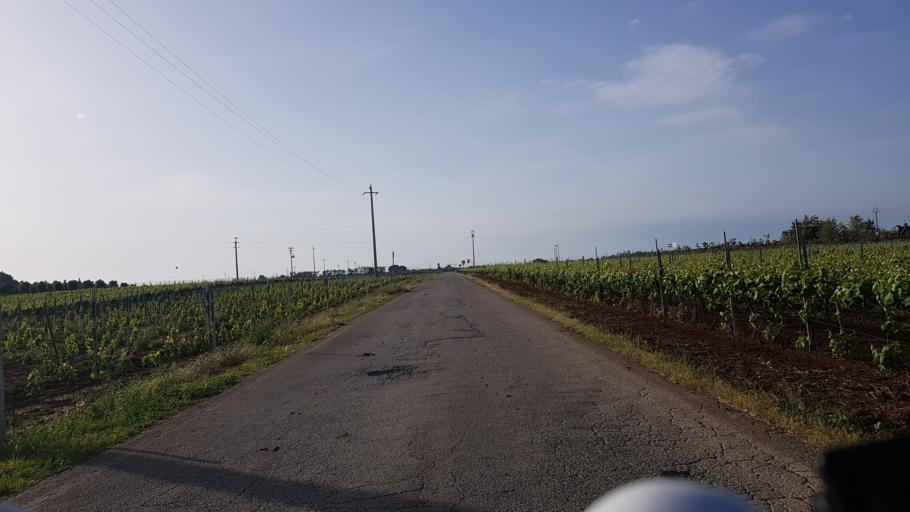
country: IT
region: Apulia
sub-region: Provincia di Brindisi
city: Mesagne
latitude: 40.5864
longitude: 17.8578
